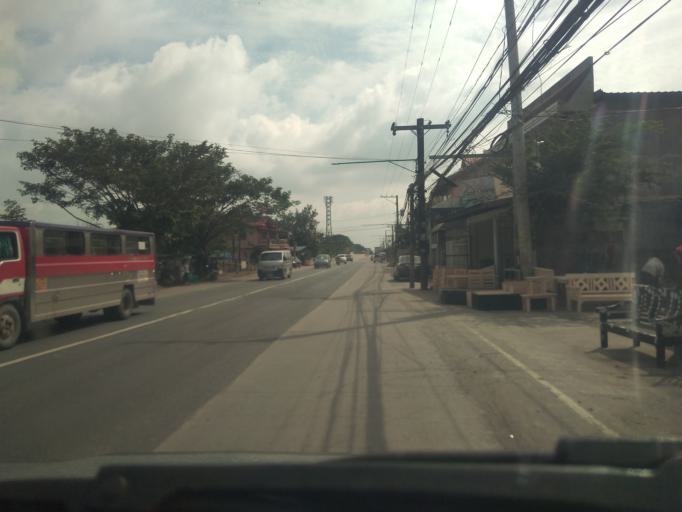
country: PH
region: Central Luzon
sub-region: Province of Pampanga
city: Pau
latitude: 15.0060
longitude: 120.7161
